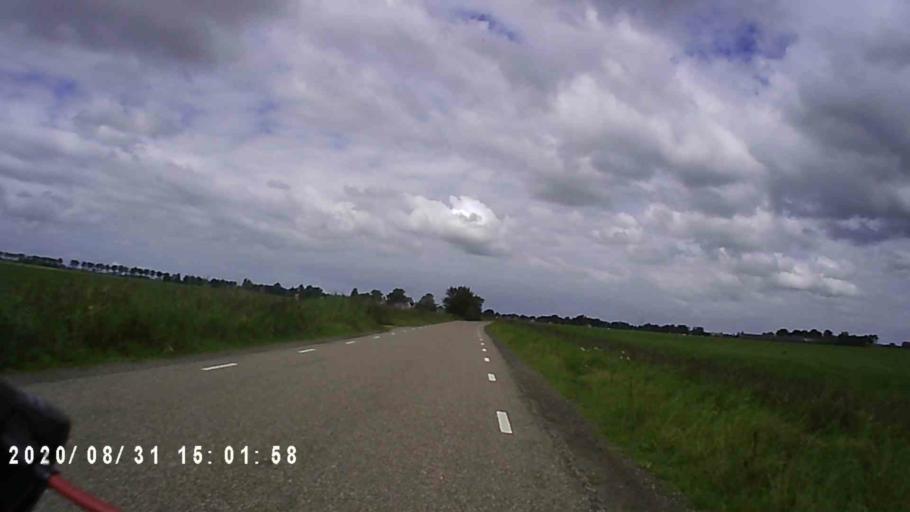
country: NL
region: Groningen
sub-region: Gemeente Zuidhorn
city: Oldehove
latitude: 53.2889
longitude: 6.3916
